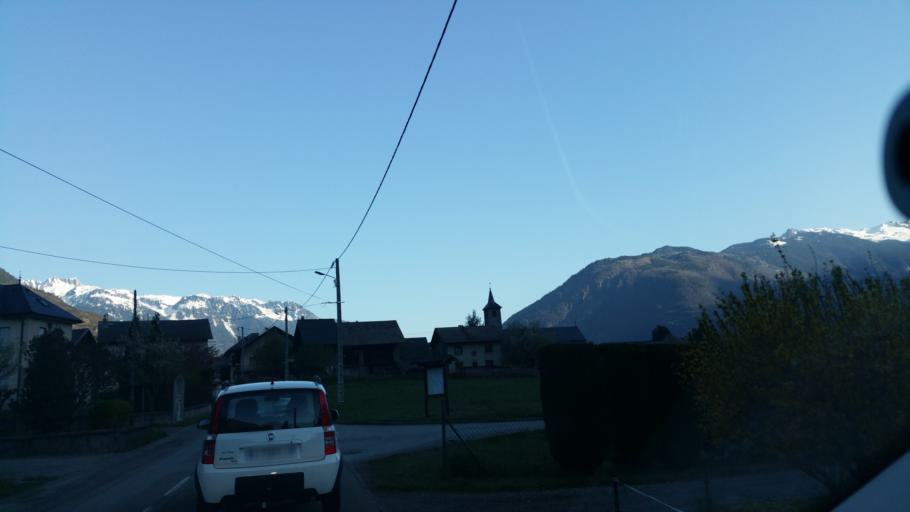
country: FR
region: Rhone-Alpes
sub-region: Departement de la Savoie
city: La Chambre
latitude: 45.3374
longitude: 6.3030
